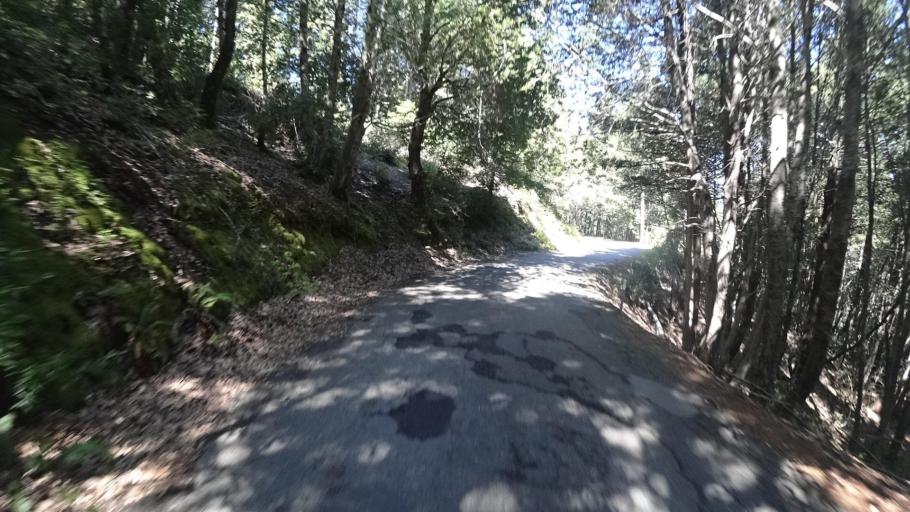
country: US
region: California
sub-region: Humboldt County
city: Redway
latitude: 40.1883
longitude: -124.0931
